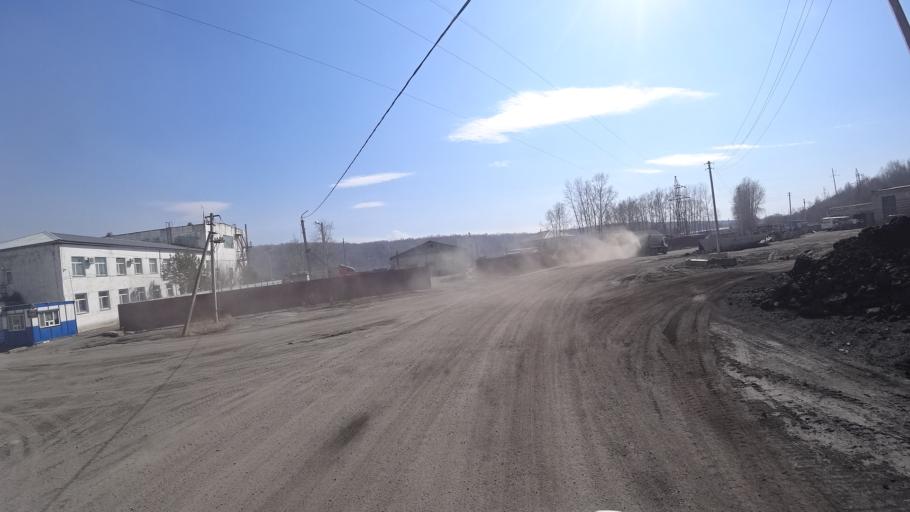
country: RU
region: Amur
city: Novobureyskiy
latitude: 49.7907
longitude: 129.9620
